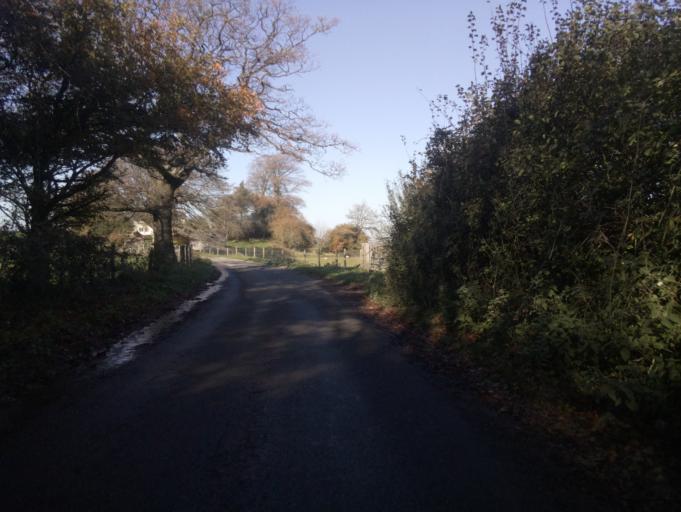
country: GB
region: England
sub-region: Dorset
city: Sherborne
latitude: 50.8508
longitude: -2.5048
